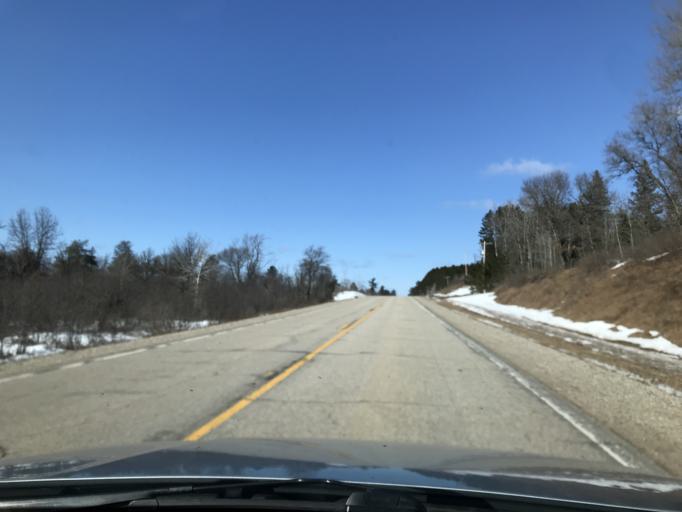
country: US
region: Wisconsin
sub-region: Marinette County
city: Niagara
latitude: 45.3756
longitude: -88.1000
